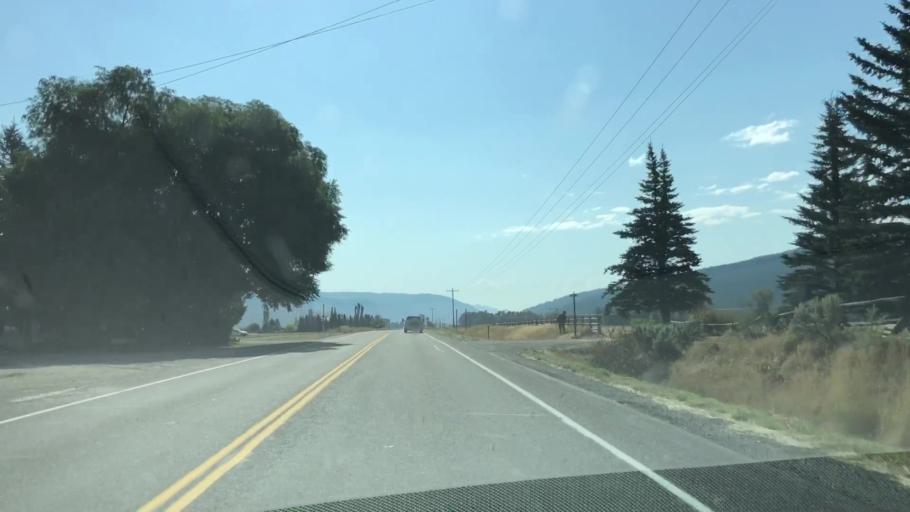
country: US
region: Idaho
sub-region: Teton County
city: Victor
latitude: 43.4006
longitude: -111.2868
